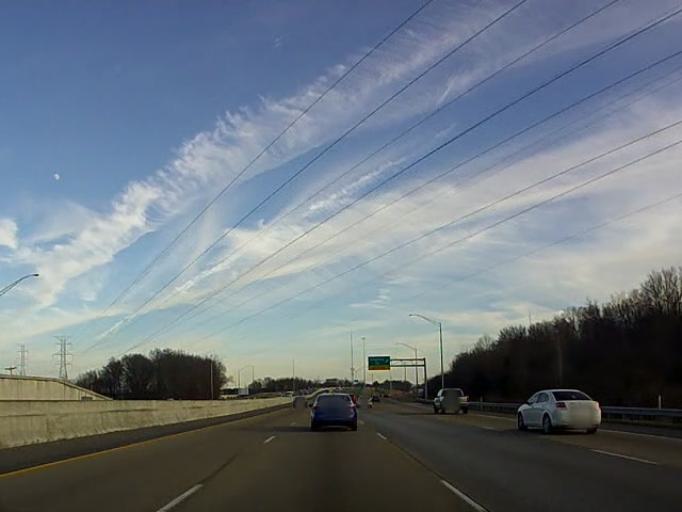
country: US
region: Tennessee
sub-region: Shelby County
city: Germantown
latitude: 35.0770
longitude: -89.8667
